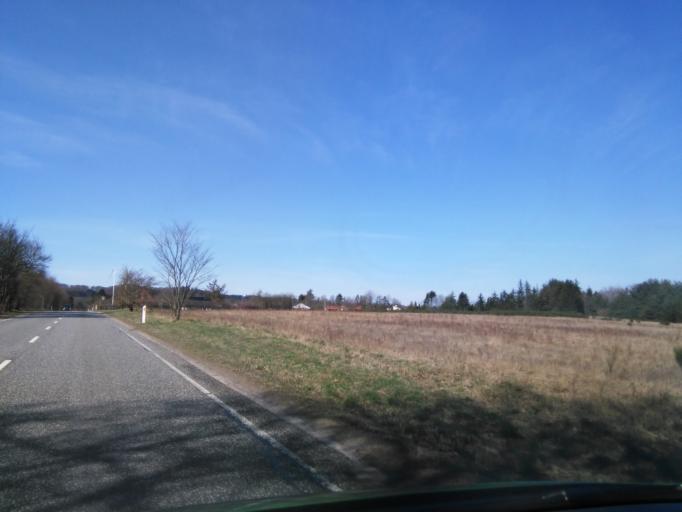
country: DK
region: Central Jutland
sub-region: Horsens Kommune
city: Braedstrup
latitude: 56.0141
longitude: 9.6923
